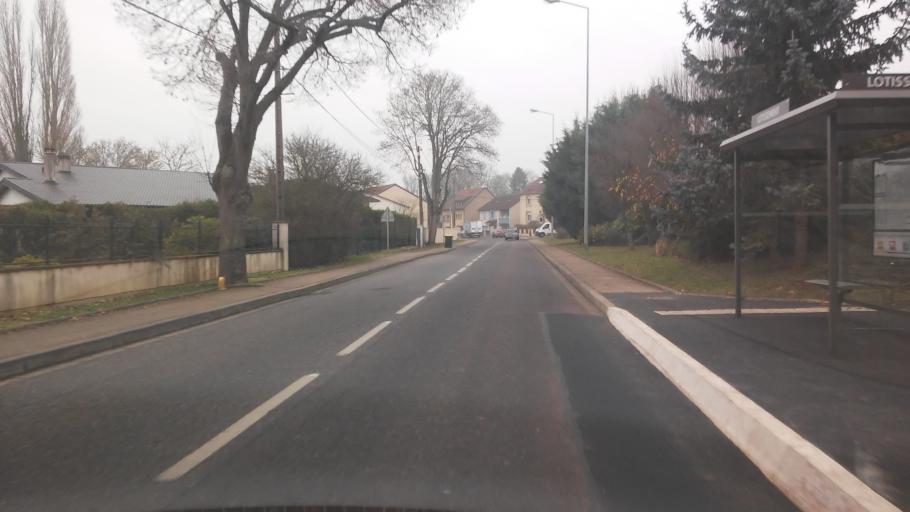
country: FR
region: Lorraine
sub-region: Departement de la Moselle
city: Augny
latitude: 49.0635
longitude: 6.1164
